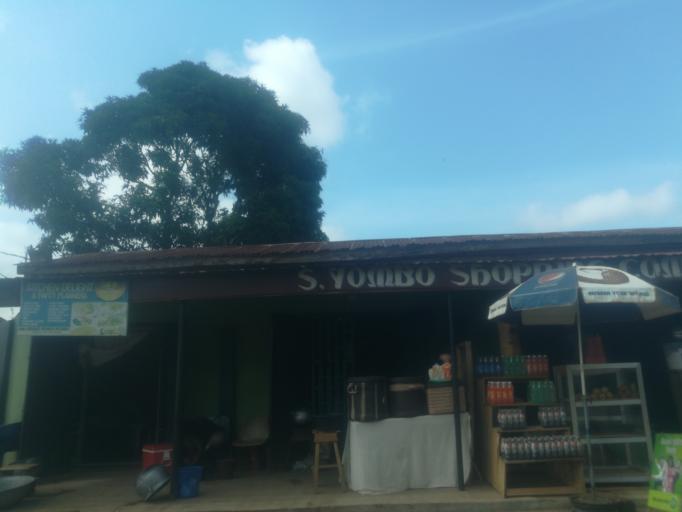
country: NG
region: Oyo
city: Ibadan
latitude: 7.3342
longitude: 3.8564
